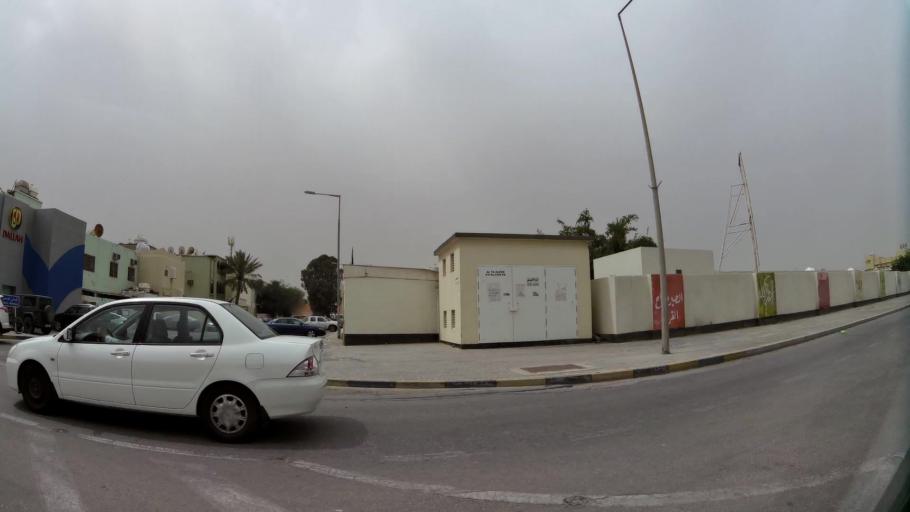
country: BH
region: Northern
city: Madinat `Isa
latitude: 26.1816
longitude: 50.5410
